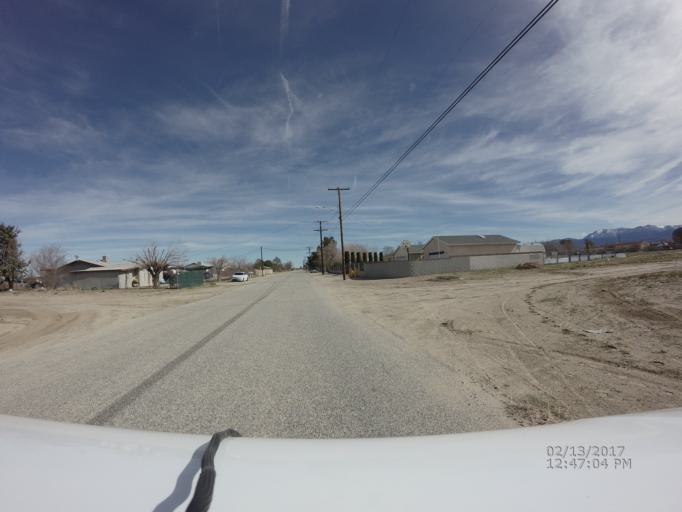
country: US
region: California
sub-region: Los Angeles County
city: Littlerock
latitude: 34.5671
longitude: -117.9299
